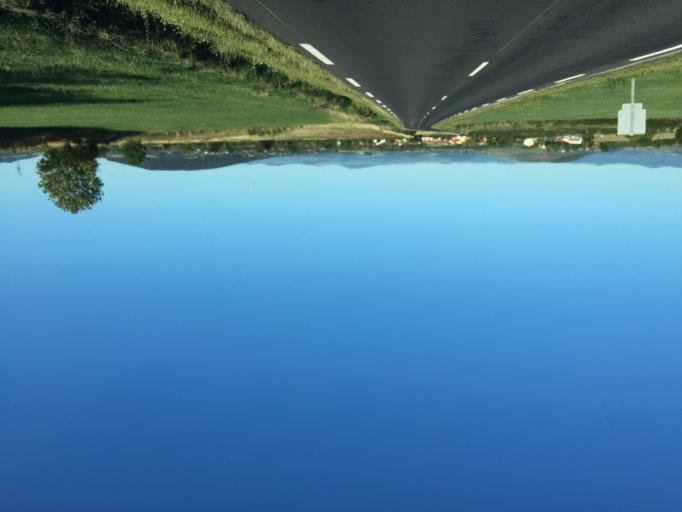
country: FR
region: Auvergne
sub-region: Departement de la Haute-Loire
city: Bains
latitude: 45.0103
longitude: 3.7891
